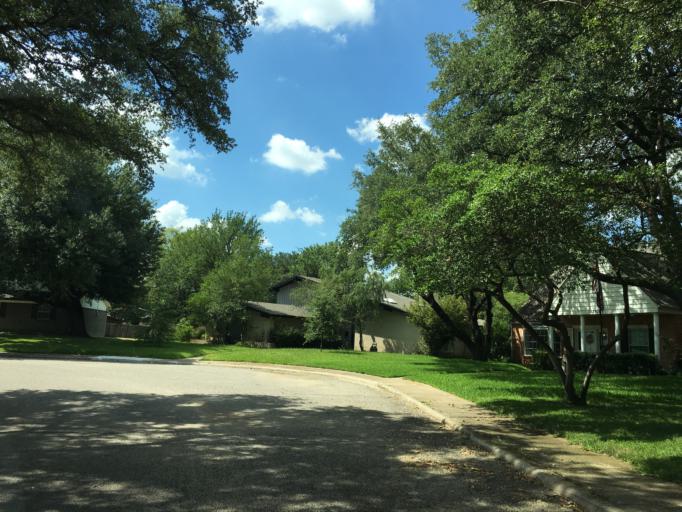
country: US
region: Texas
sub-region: Dallas County
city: Farmers Branch
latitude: 32.9229
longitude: -96.8600
